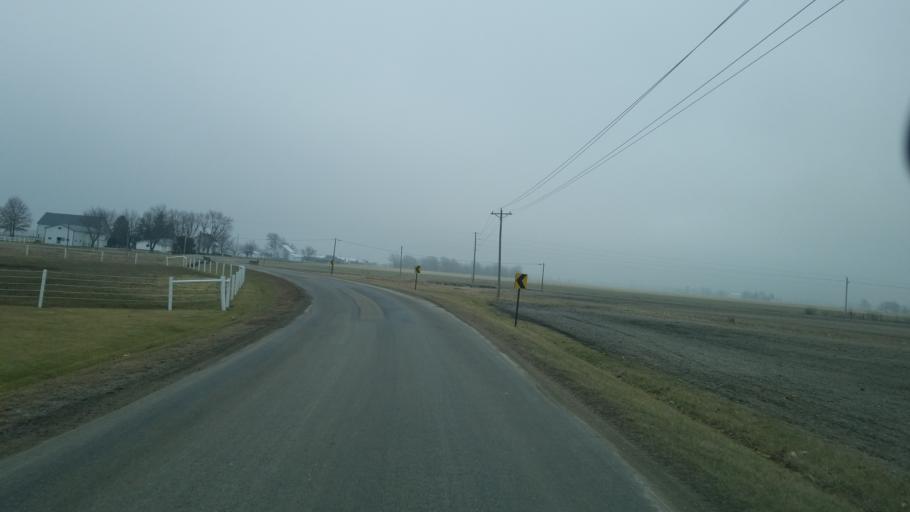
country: US
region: Indiana
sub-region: Adams County
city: Berne
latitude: 40.7000
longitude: -84.9965
